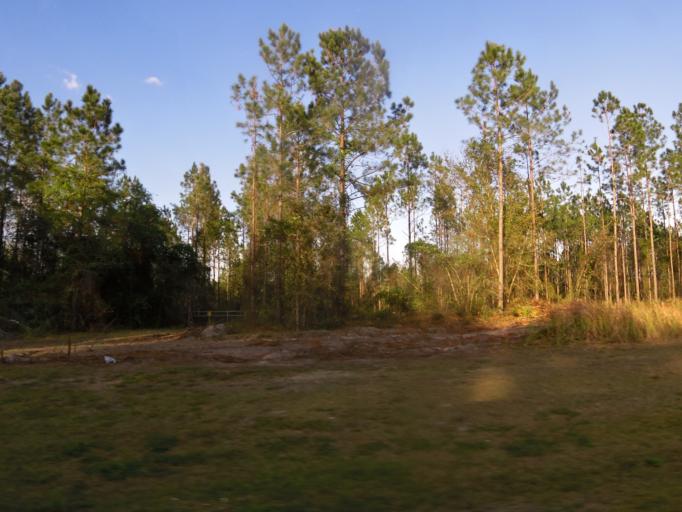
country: US
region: Florida
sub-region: Saint Johns County
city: Fruit Cove
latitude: 30.0825
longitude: -81.5293
